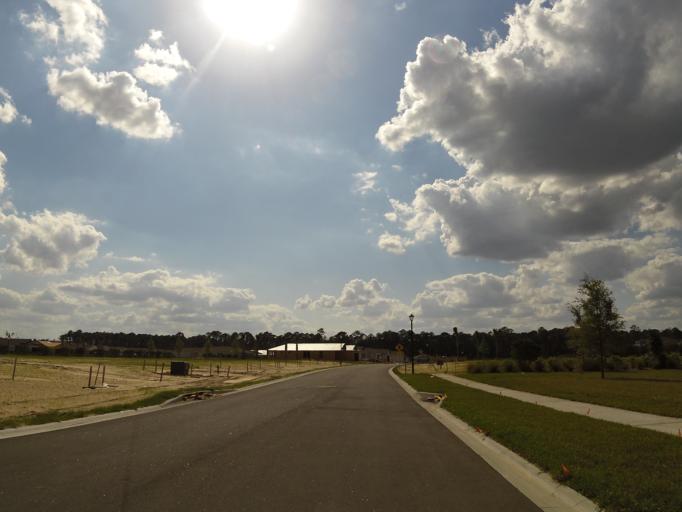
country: US
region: Florida
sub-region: Saint Johns County
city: Palm Valley
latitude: 30.1732
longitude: -81.5072
